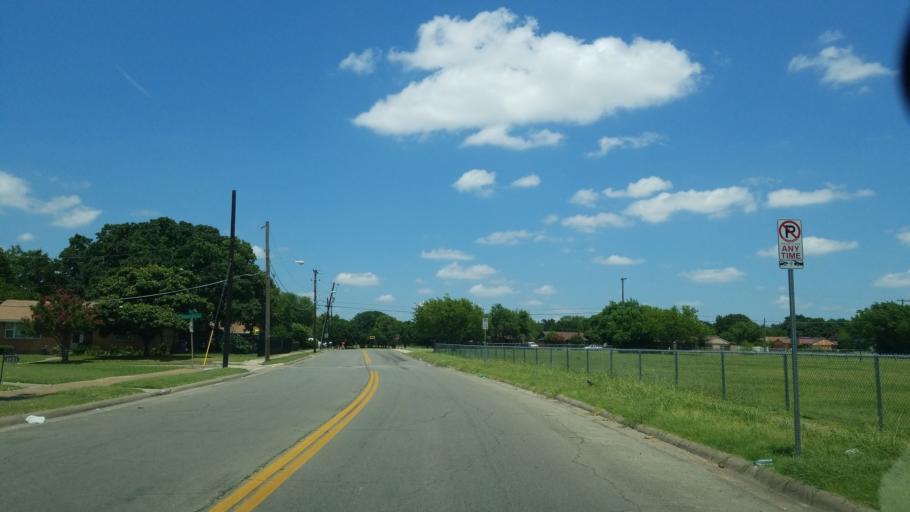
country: US
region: Texas
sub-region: Dallas County
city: Balch Springs
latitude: 32.7399
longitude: -96.7027
